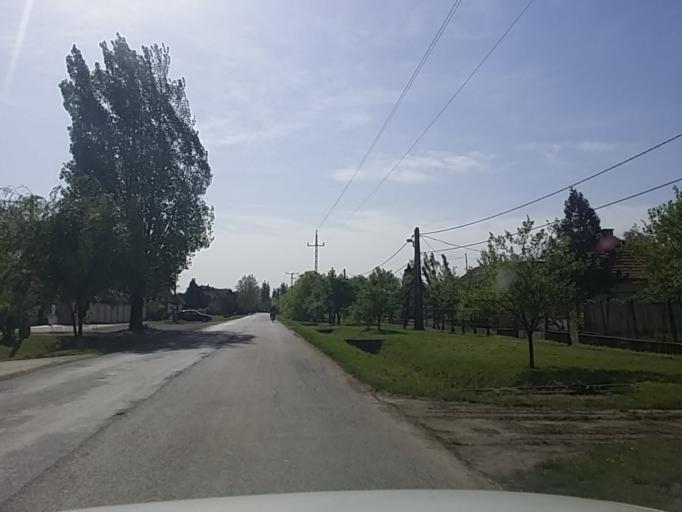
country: HU
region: Bekes
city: Doboz
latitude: 46.7034
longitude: 21.1818
